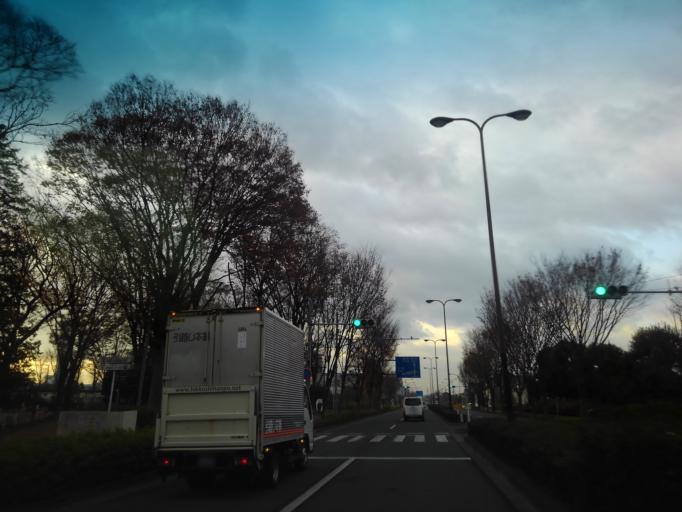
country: JP
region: Tokyo
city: Kokubunji
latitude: 35.6894
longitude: 139.4599
